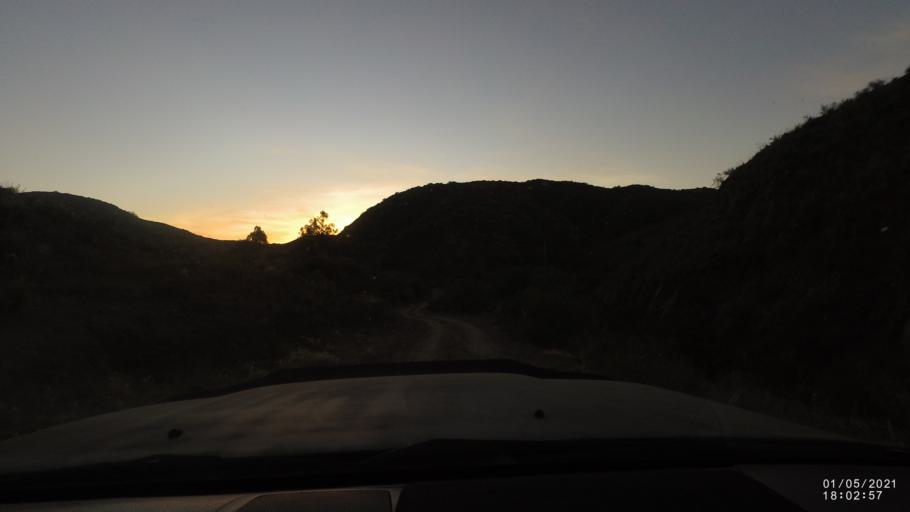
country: BO
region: Cochabamba
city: Capinota
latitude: -17.6890
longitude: -66.1749
